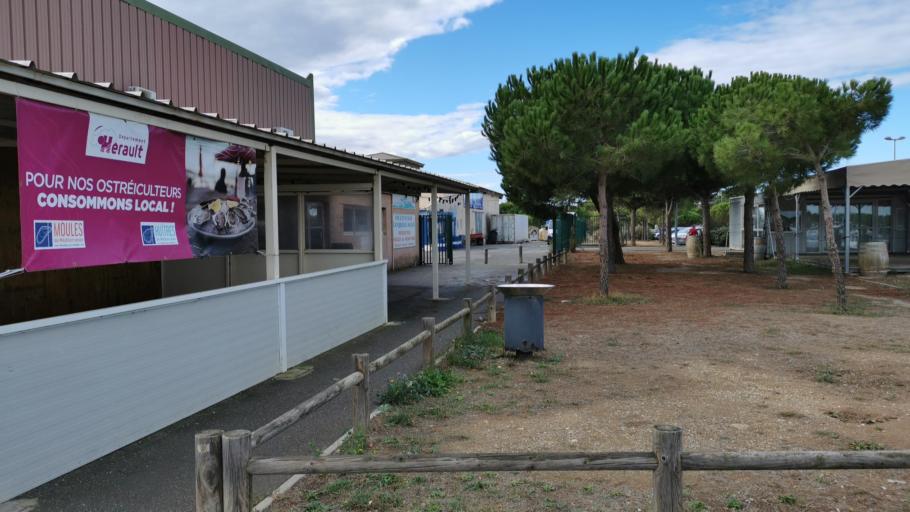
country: FR
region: Languedoc-Roussillon
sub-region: Departement de l'Herault
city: Vendres
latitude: 43.2190
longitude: 3.2335
